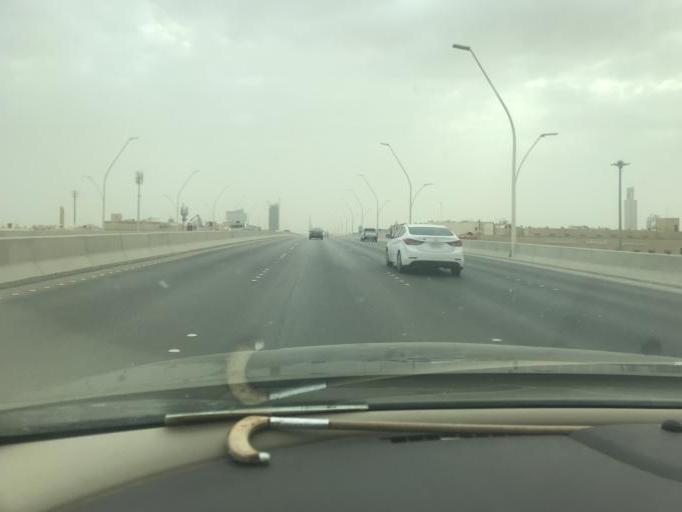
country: SA
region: Ar Riyad
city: Riyadh
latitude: 24.8196
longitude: 46.6445
